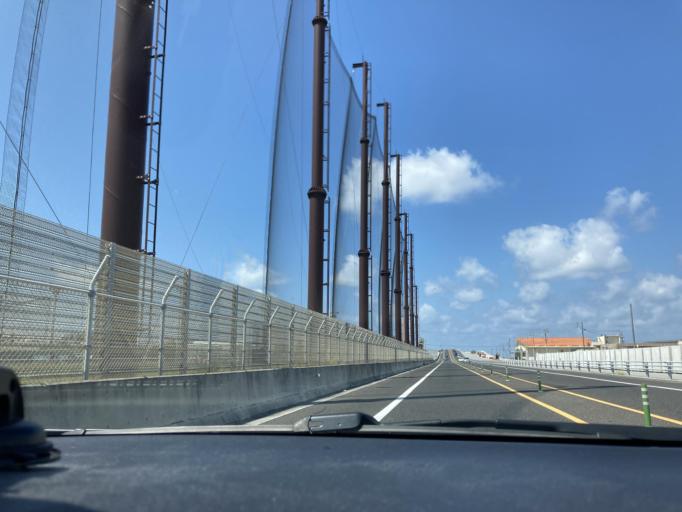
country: JP
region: Okinawa
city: Ginowan
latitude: 26.2727
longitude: 127.7168
